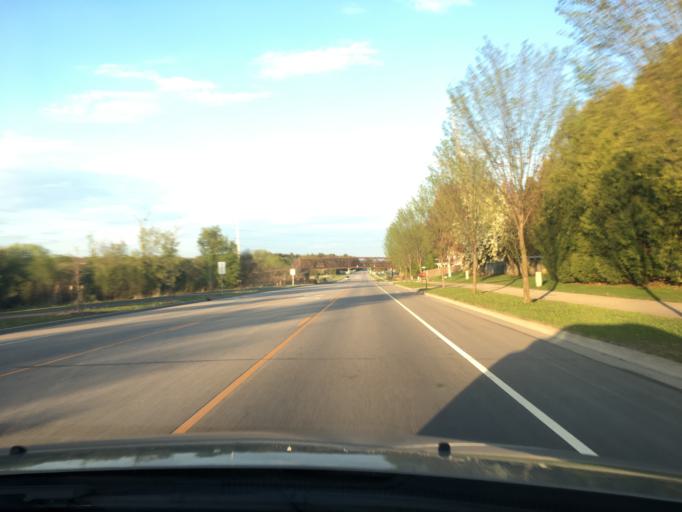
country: US
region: Minnesota
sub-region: Olmsted County
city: Oronoco
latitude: 44.0793
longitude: -92.5360
